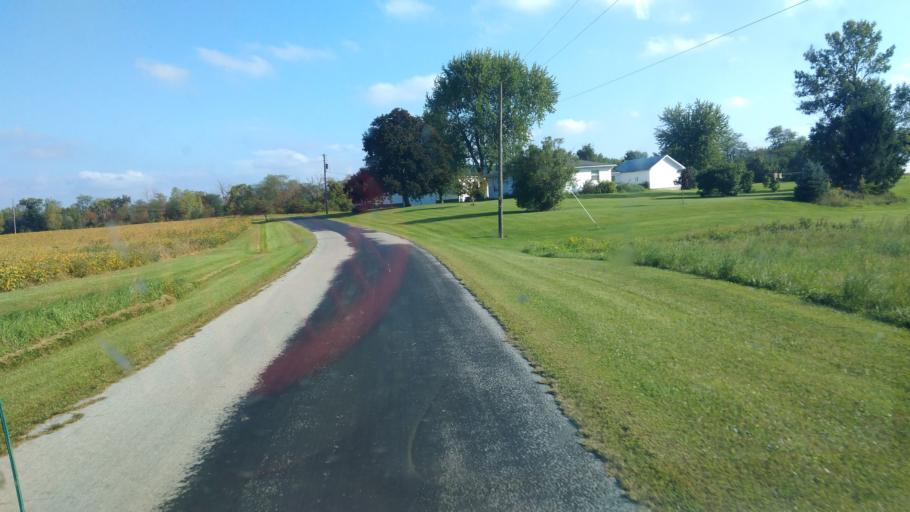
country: US
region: Ohio
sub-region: Hardin County
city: Forest
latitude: 40.7194
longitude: -83.4590
